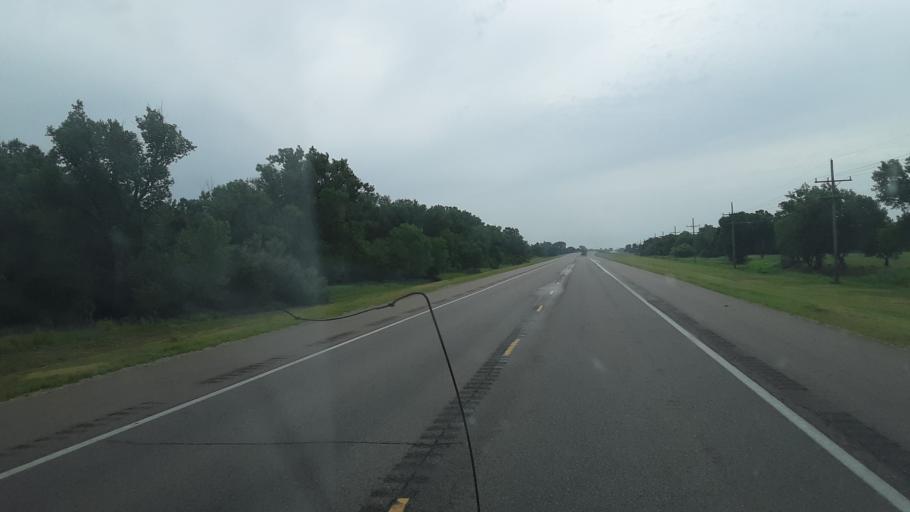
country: US
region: Kansas
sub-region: Edwards County
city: Kinsley
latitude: 37.9279
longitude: -99.3831
